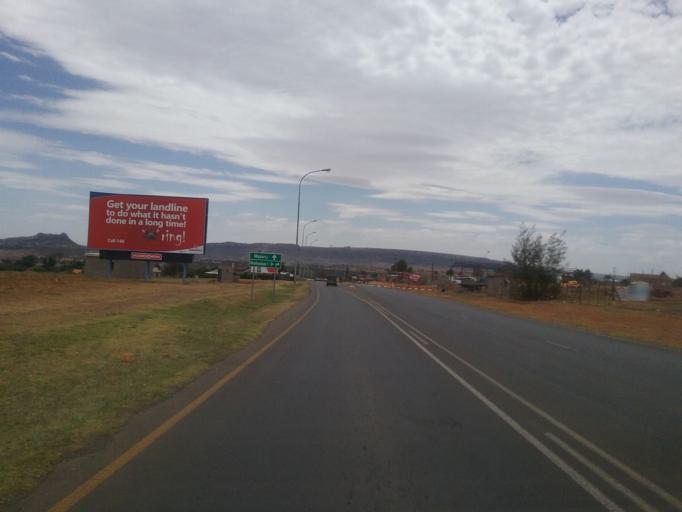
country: LS
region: Maseru
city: Maseru
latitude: -29.4246
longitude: 27.5618
